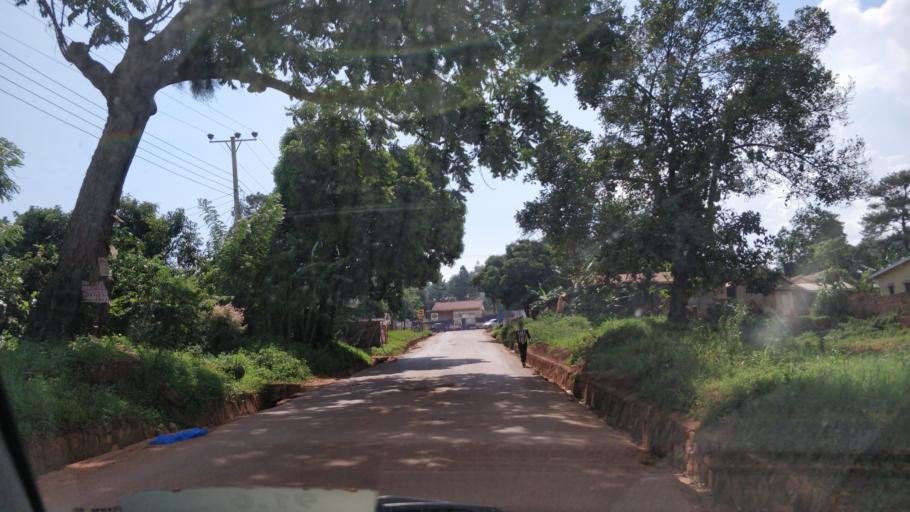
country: UG
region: Central Region
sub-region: Kampala District
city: Kampala
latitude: 0.2682
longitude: 32.6152
